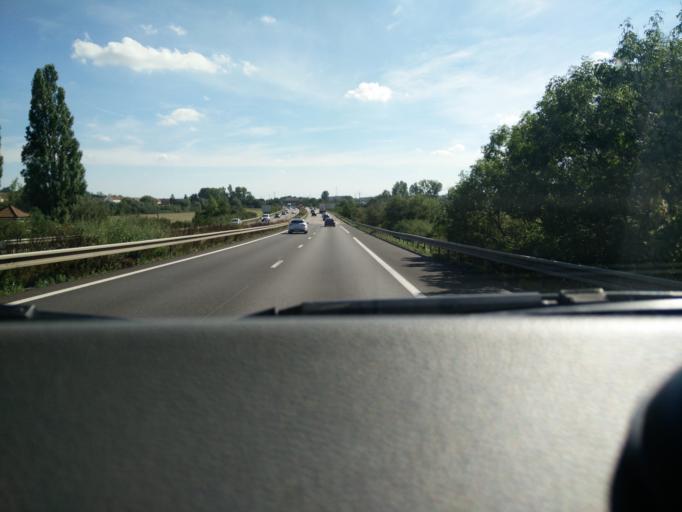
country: FR
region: Lorraine
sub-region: Departement de la Moselle
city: Bertrange
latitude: 49.3163
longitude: 6.1825
